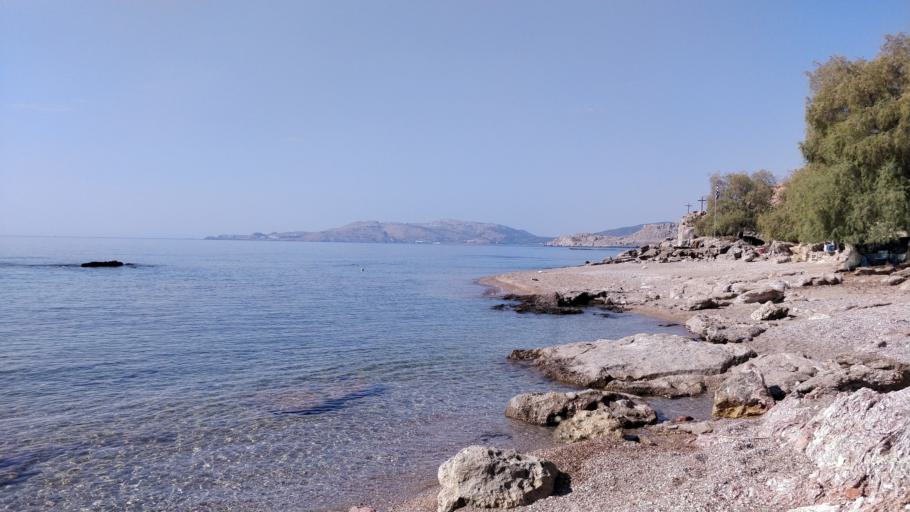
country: GR
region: South Aegean
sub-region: Nomos Dodekanisou
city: Archangelos
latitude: 36.1873
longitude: 28.1217
